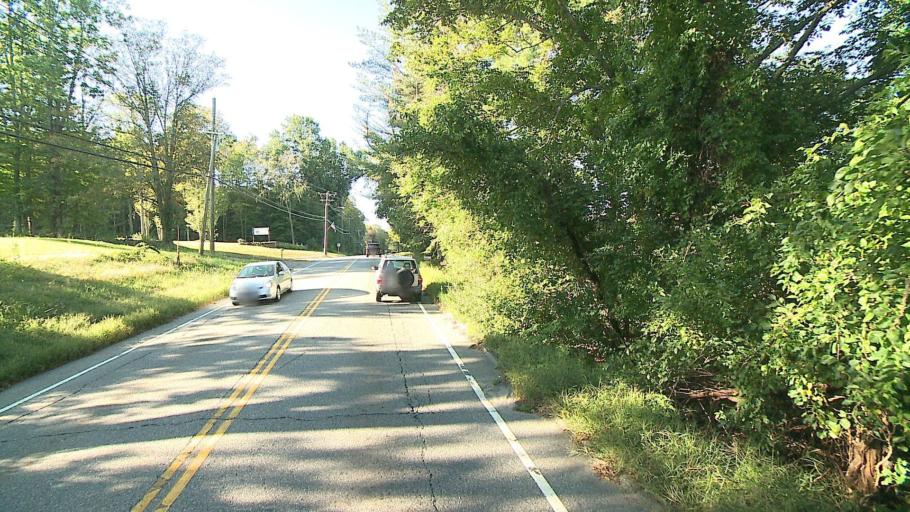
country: US
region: Connecticut
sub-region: Windham County
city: Plainfield
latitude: 41.6951
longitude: -71.9093
